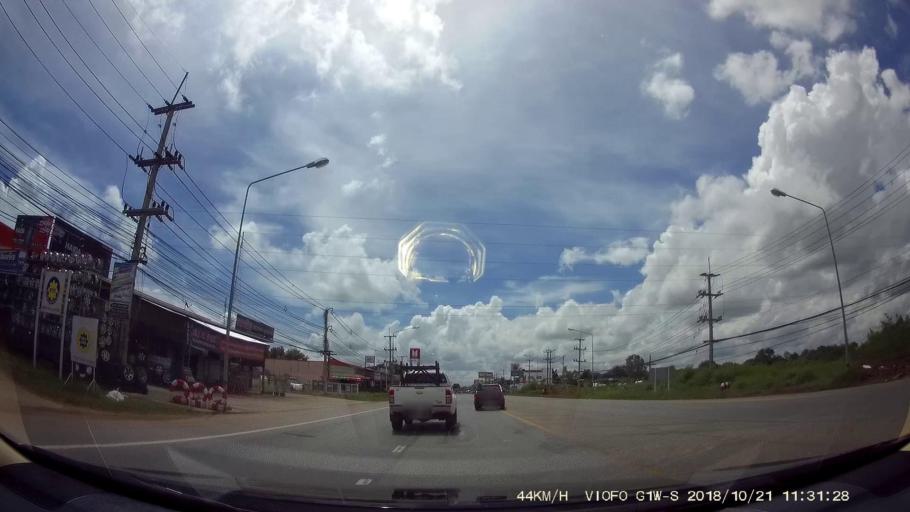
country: TH
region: Chaiyaphum
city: Chaiyaphum
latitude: 15.7689
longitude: 102.0259
